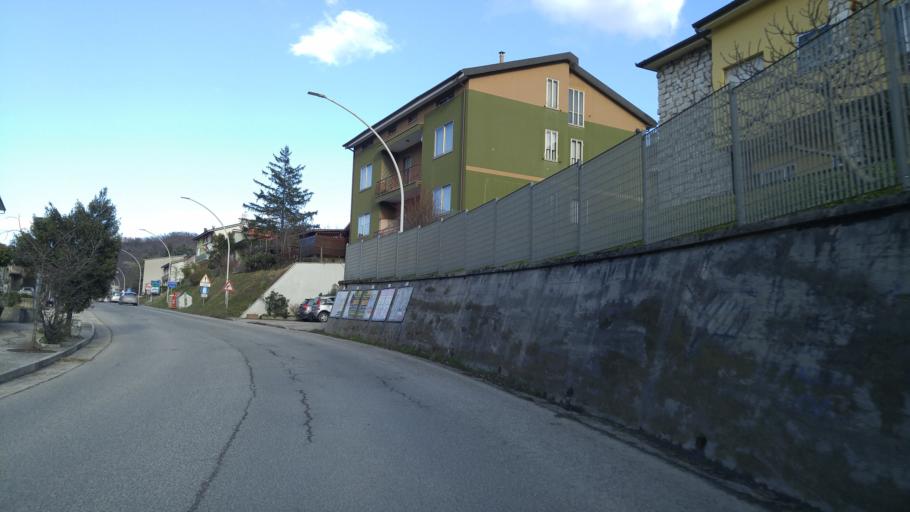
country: IT
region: The Marches
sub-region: Provincia di Pesaro e Urbino
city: Cagli
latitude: 43.5453
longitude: 12.6529
